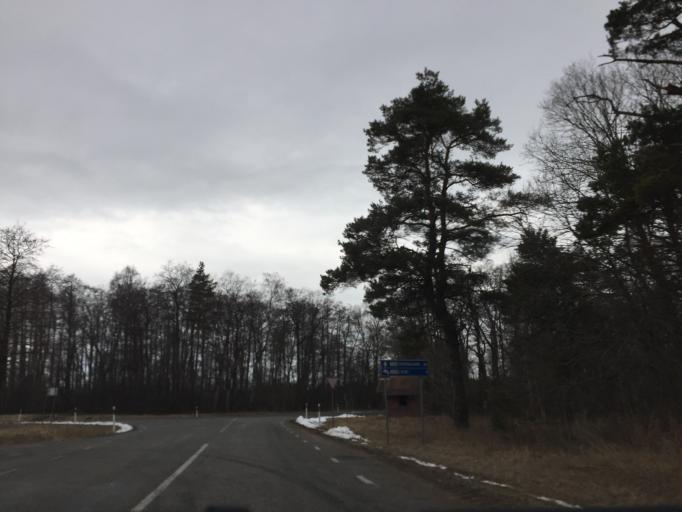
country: EE
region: Saare
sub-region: Orissaare vald
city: Orissaare
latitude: 58.5686
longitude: 22.7620
